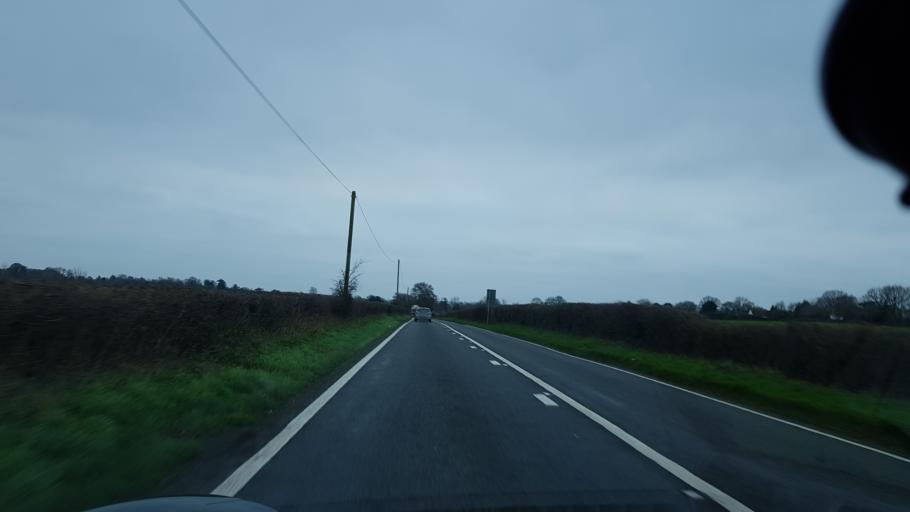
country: GB
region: England
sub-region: Somerset
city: Chard
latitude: 50.9006
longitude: -2.9479
